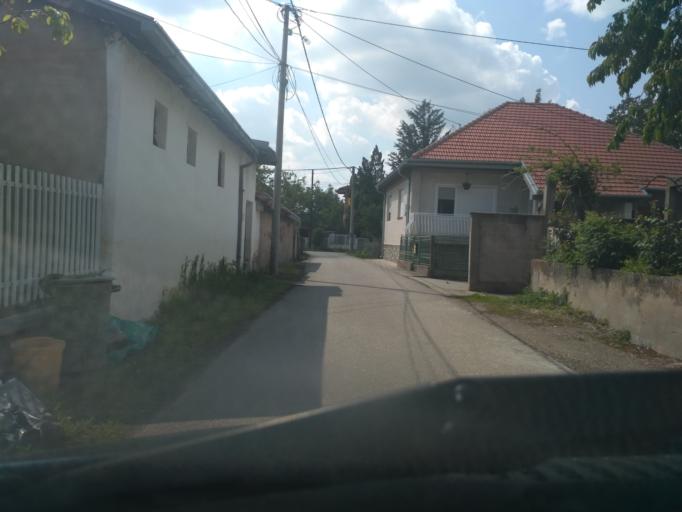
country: RS
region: Central Serbia
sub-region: Pomoravski Okrug
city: Svilajnac
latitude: 44.2353
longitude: 21.2029
